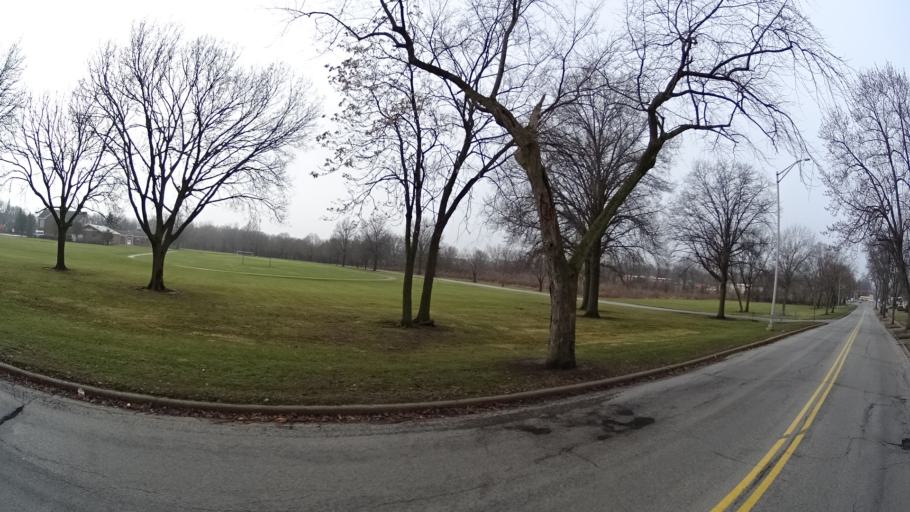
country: US
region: Illinois
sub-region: Cook County
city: East Hazel Crest
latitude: 41.5497
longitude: -87.6320
